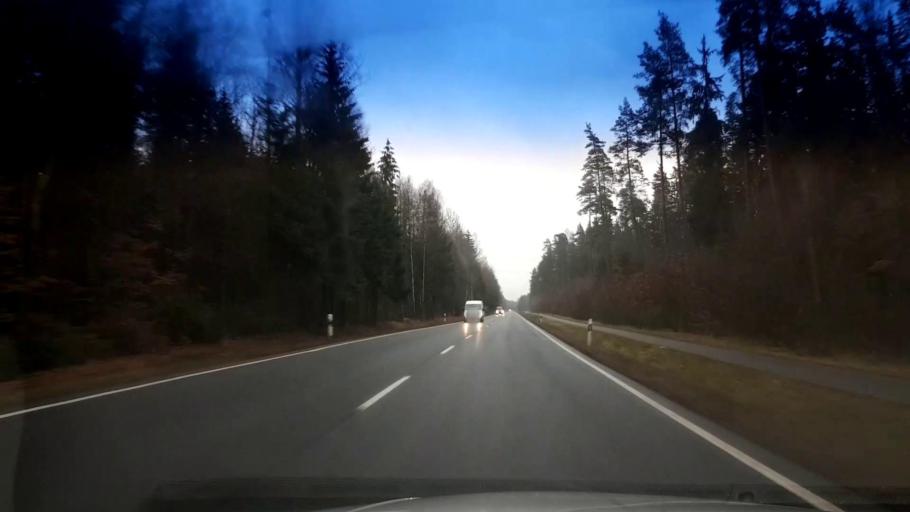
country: DE
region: Bavaria
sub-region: Upper Palatinate
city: Leonberg
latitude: 49.9213
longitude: 12.2891
